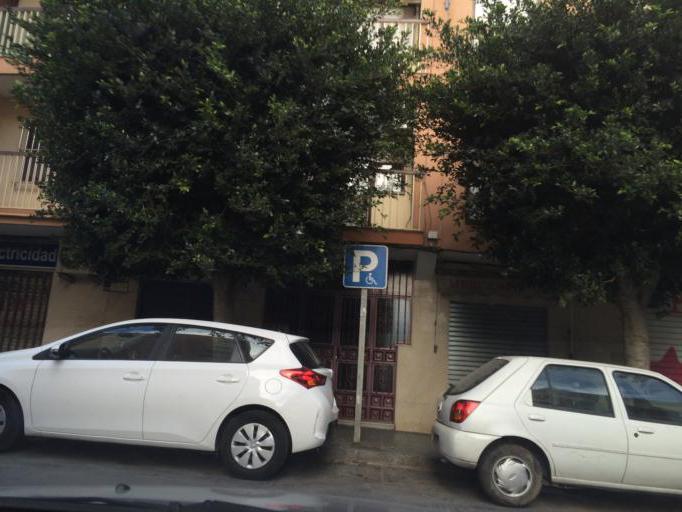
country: ES
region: Andalusia
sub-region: Provincia de Almeria
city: Almeria
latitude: 36.8392
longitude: -2.4733
